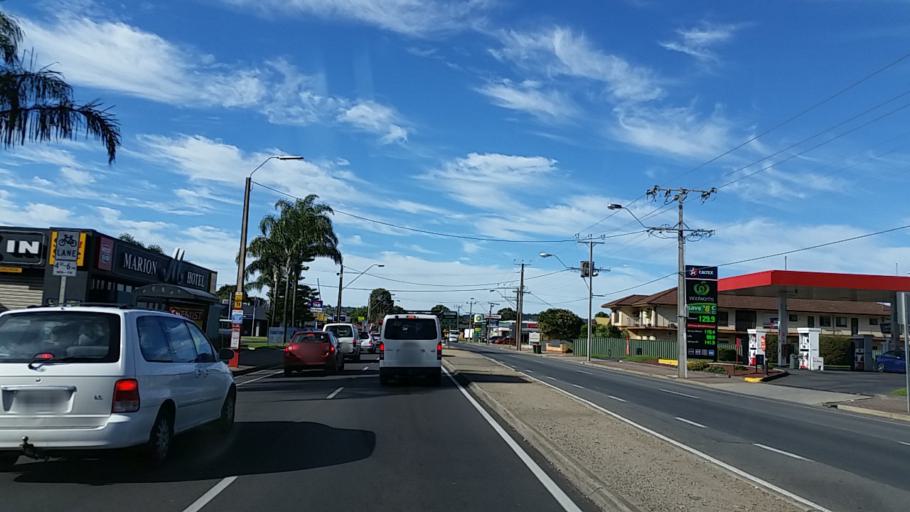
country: AU
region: South Australia
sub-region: Marion
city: Clovelly Park
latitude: -35.0038
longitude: 138.5578
